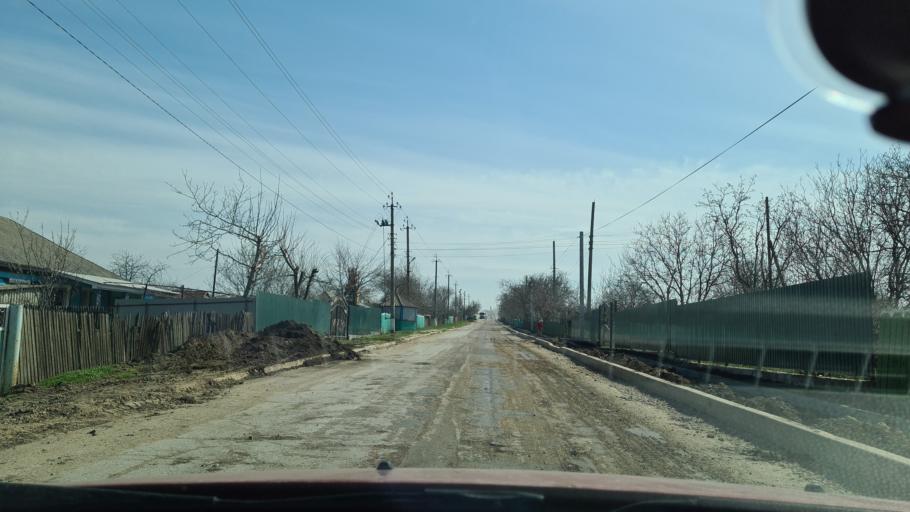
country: MD
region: Ungheni
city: Ungheni
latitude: 47.2689
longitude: 27.9448
